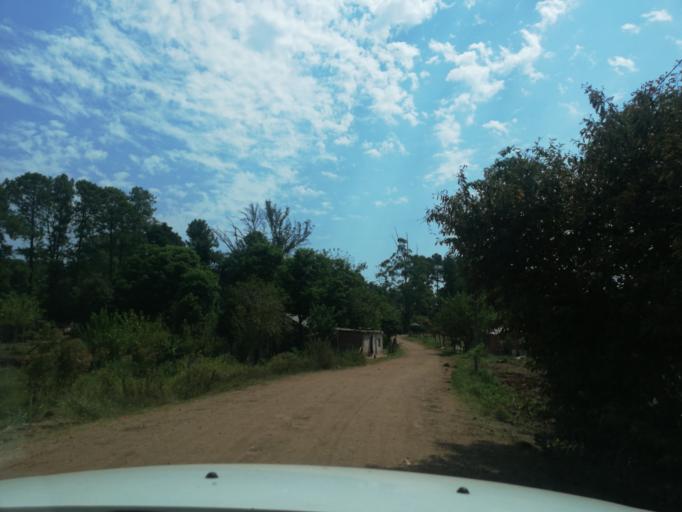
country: AR
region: Misiones
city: Garupa
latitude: -27.4482
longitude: -55.8928
